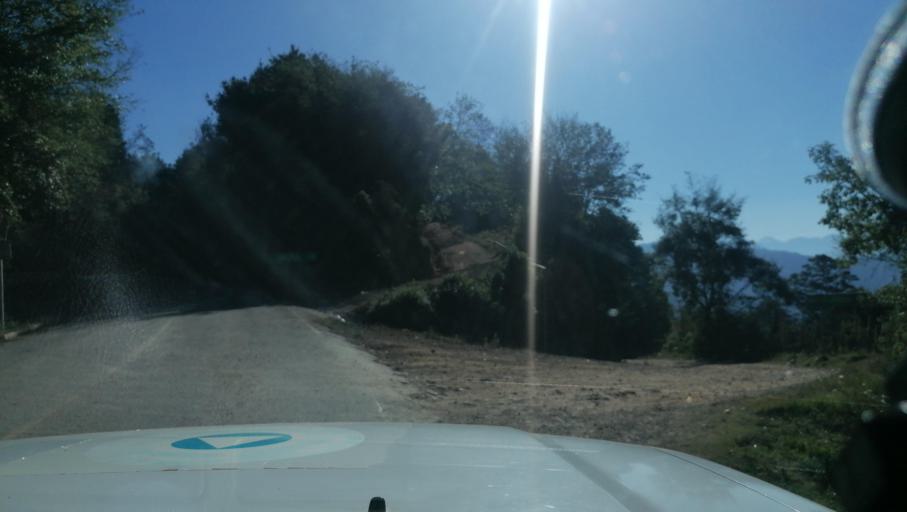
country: MX
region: Chiapas
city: Motozintla de Mendoza
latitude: 15.2539
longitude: -92.2173
